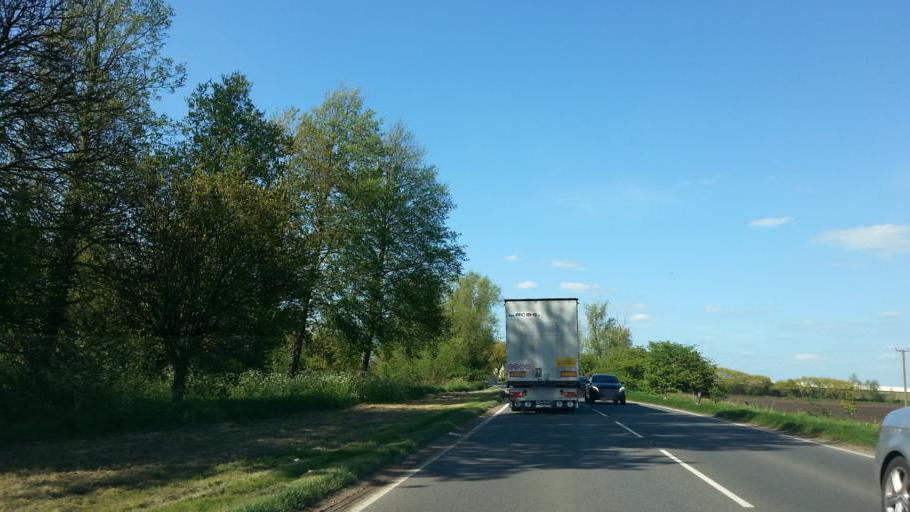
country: GB
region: England
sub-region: Cambridgeshire
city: Stretham
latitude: 52.3179
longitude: 0.1986
